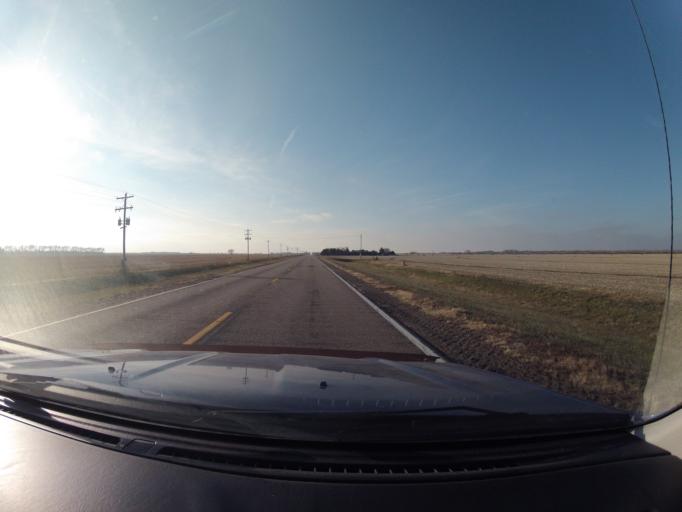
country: US
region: Nebraska
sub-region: Buffalo County
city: Kearney
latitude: 40.6411
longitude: -99.0501
